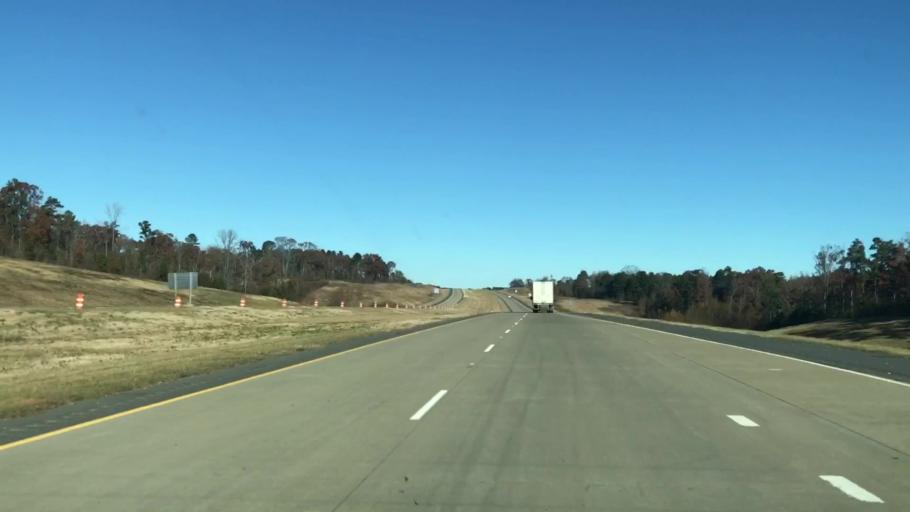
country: US
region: Louisiana
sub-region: Caddo Parish
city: Vivian
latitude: 32.9492
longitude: -93.8988
